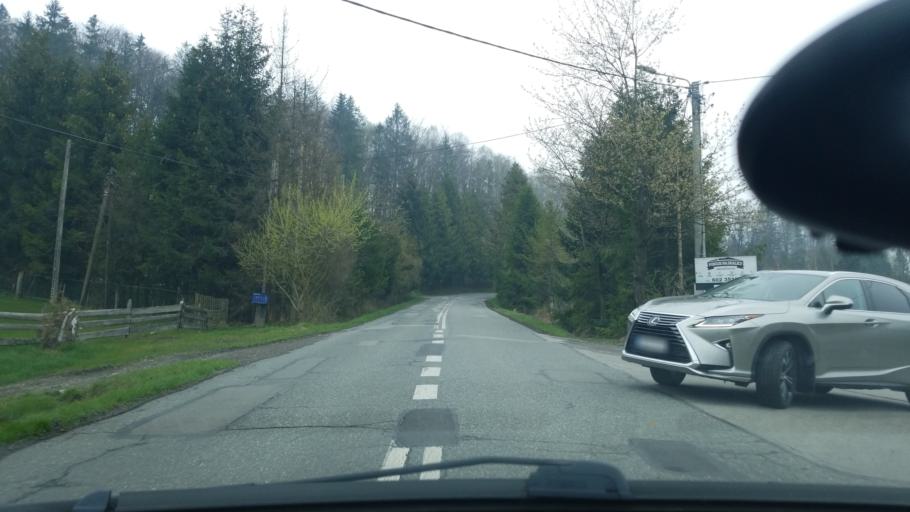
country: PL
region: Silesian Voivodeship
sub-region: Powiat cieszynski
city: Ustron
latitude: 49.7049
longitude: 18.8342
